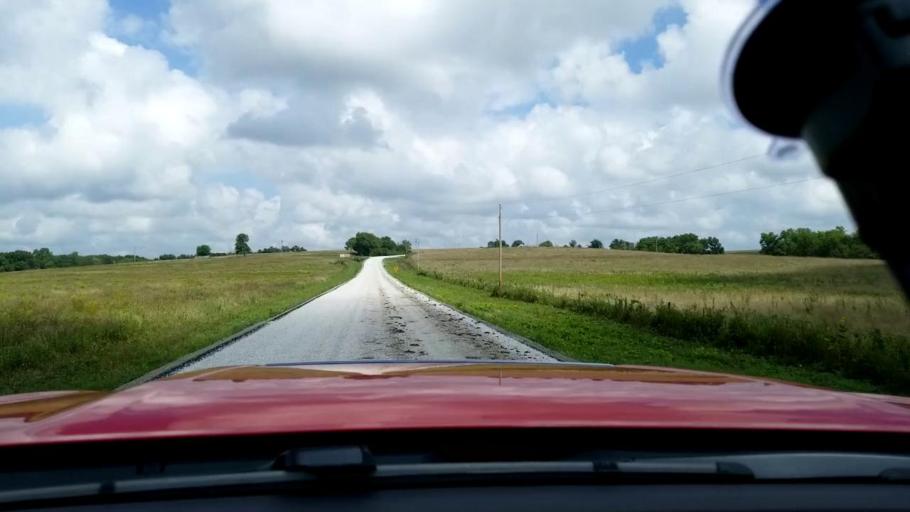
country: US
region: Iowa
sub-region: Decatur County
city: Lamoni
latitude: 40.6496
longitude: -94.0531
